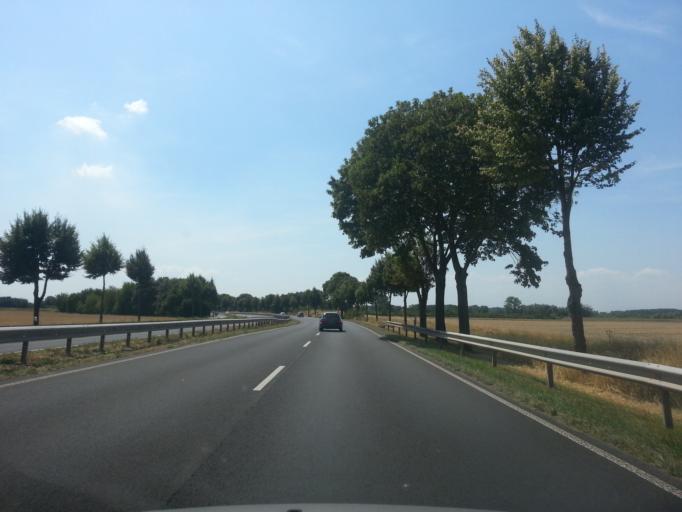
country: DE
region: Hesse
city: Lampertheim
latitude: 49.5869
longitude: 8.4517
